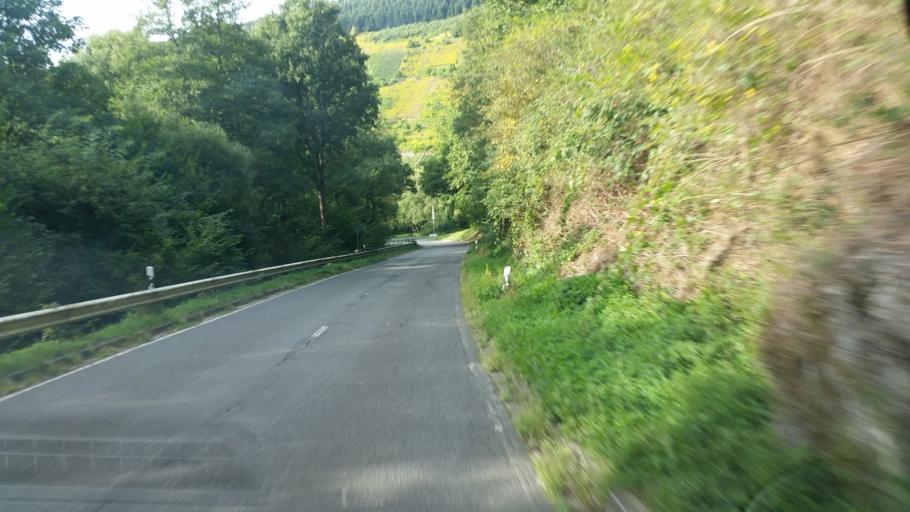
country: DE
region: Rheinland-Pfalz
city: Starkenburg
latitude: 49.9808
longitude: 7.1457
